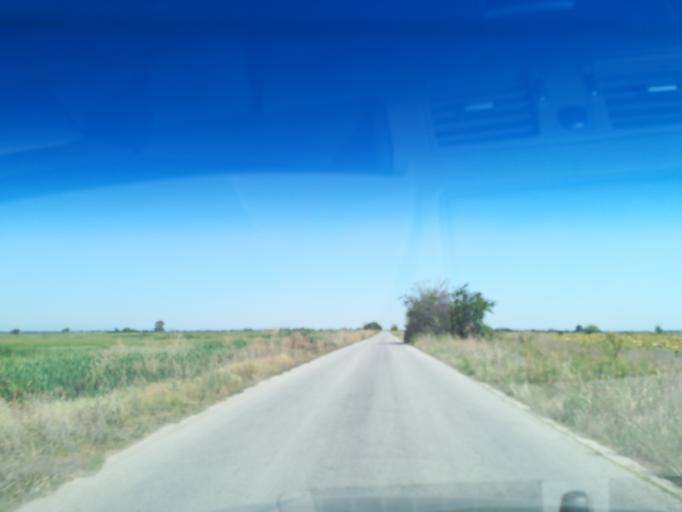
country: BG
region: Plovdiv
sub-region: Obshtina Suedinenie
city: Suedinenie
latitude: 42.2512
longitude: 24.4799
